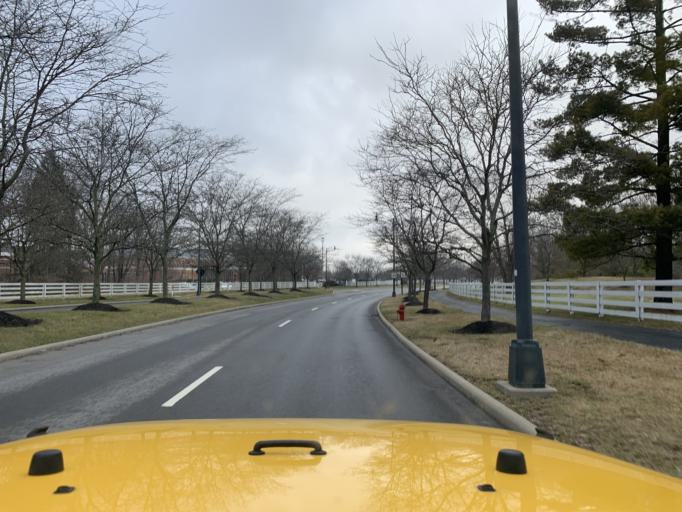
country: US
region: Ohio
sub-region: Franklin County
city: New Albany
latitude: 40.0854
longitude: -82.7878
